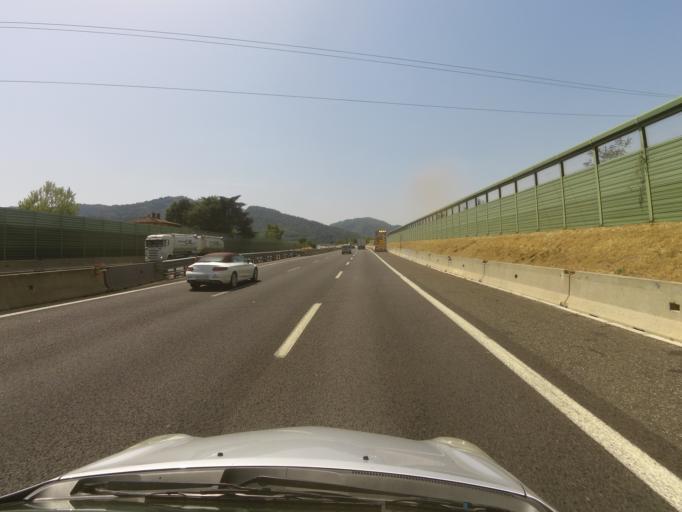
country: IT
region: Emilia-Romagna
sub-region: Provincia di Bologna
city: Sasso Marconi
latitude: 44.4016
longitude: 11.2624
